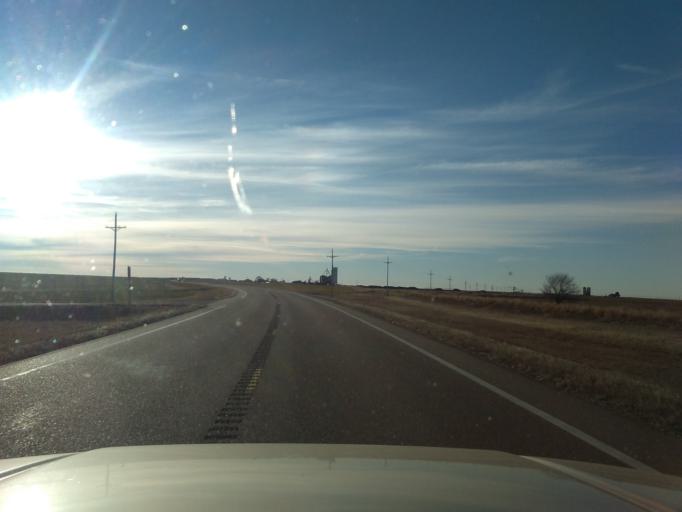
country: US
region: Kansas
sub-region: Thomas County
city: Colby
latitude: 39.4530
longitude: -100.8012
